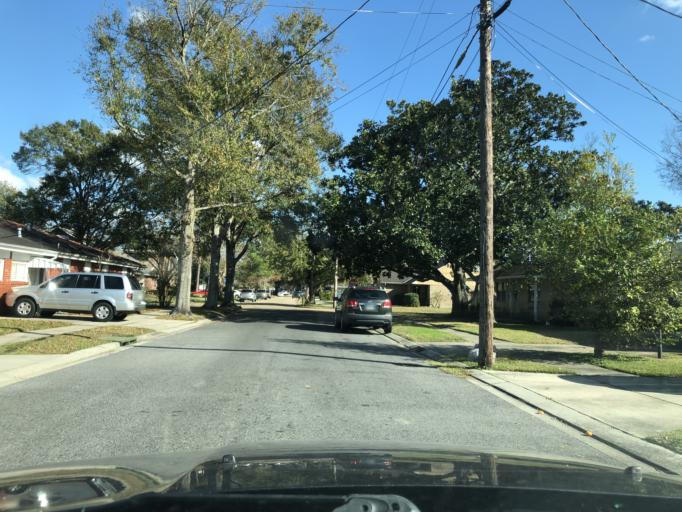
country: US
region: Louisiana
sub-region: Jefferson Parish
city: Metairie Terrace
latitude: 29.9854
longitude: -90.1620
